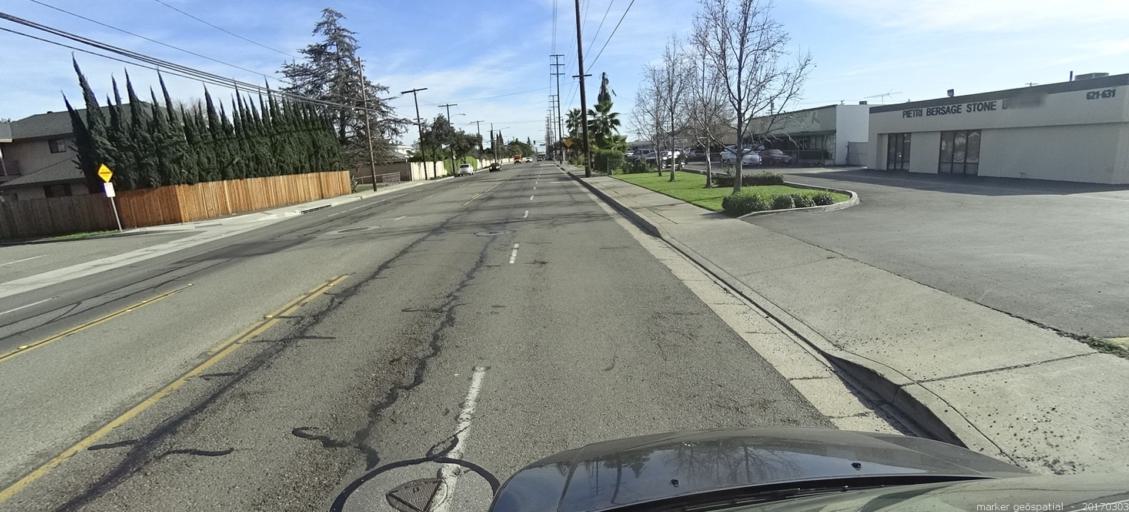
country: US
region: California
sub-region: Orange County
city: Anaheim
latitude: 33.8309
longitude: -117.9004
